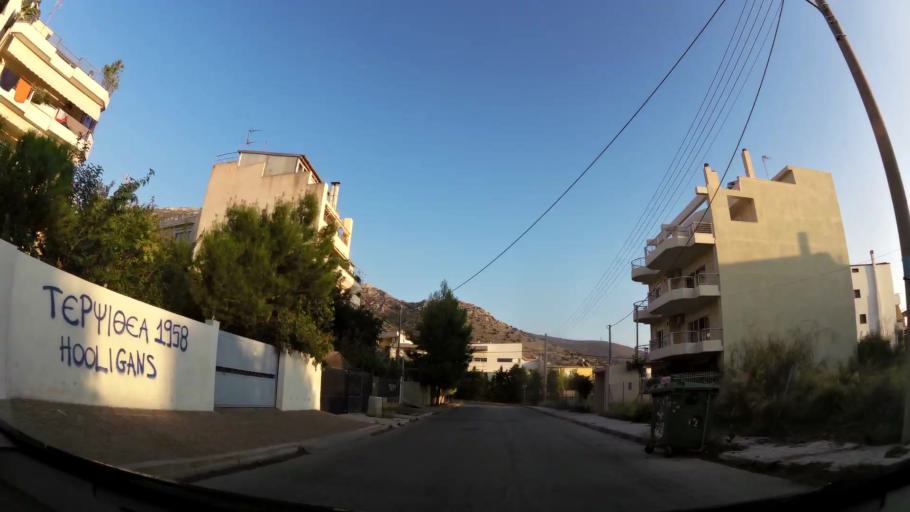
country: GR
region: Attica
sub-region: Nomarchia Athinas
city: Glyfada
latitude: 37.8831
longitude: 23.7712
